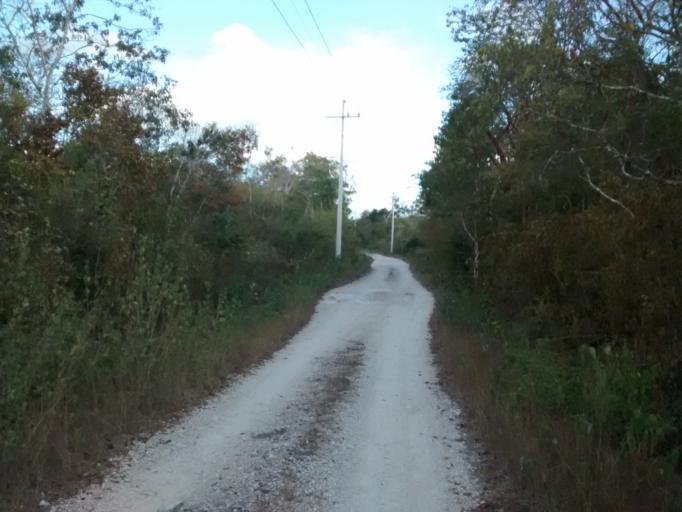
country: MX
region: Yucatan
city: Chichimila
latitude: 20.4487
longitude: -88.2014
